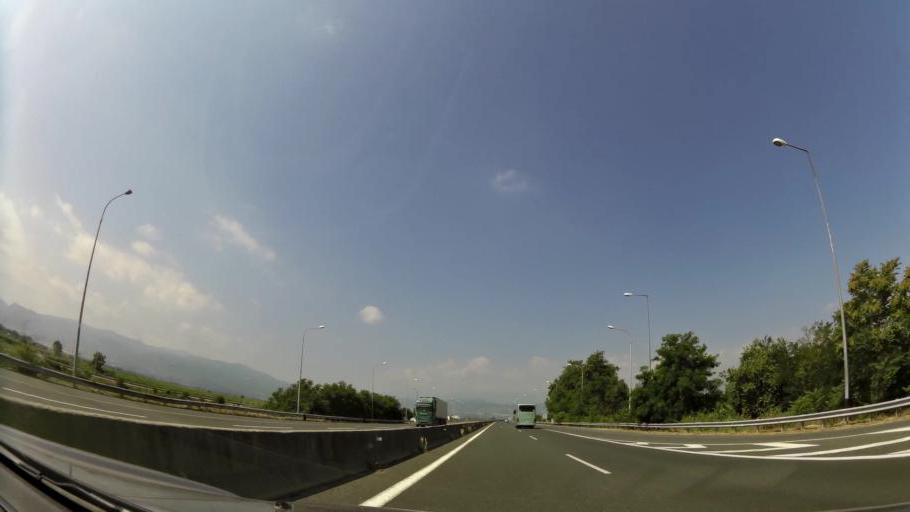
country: GR
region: Central Macedonia
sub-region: Nomos Imathias
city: Kouloura
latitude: 40.5408
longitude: 22.3158
